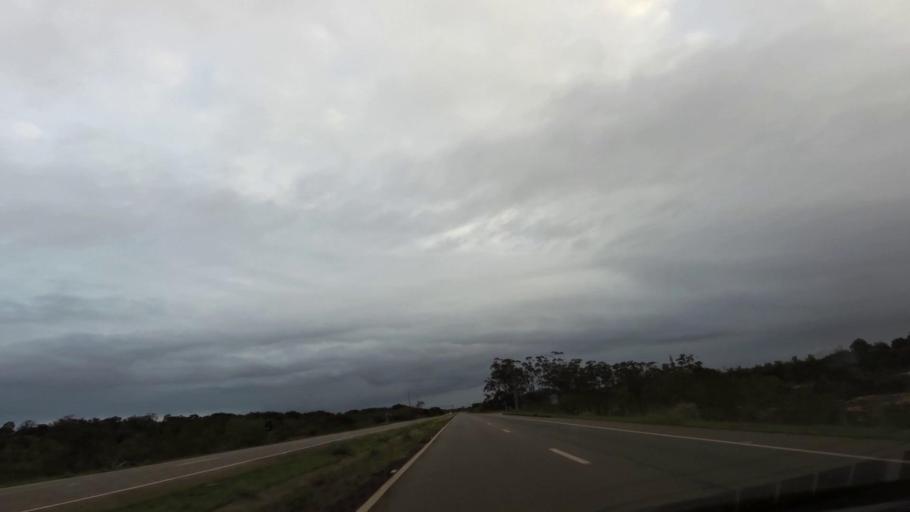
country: BR
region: Espirito Santo
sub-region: Guarapari
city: Guarapari
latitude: -20.5956
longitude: -40.4257
